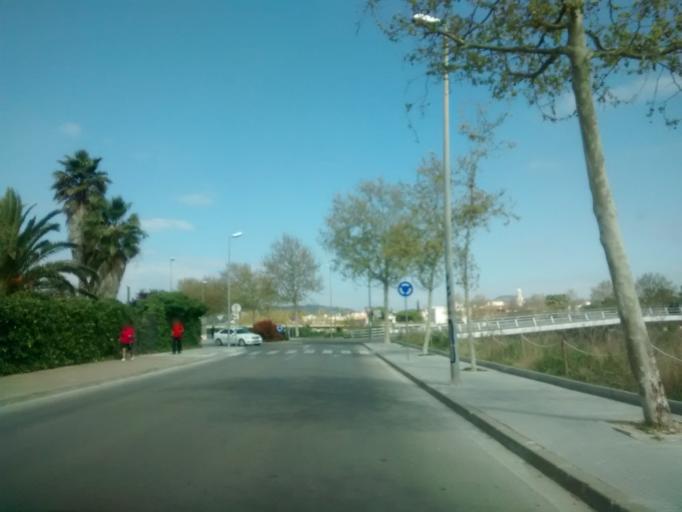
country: ES
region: Catalonia
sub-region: Provincia de Barcelona
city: Cubelles
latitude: 41.2012
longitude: 1.6734
